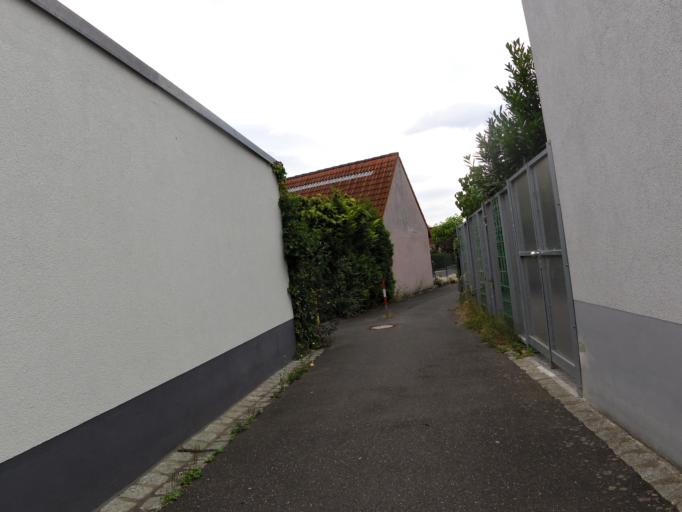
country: DE
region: Bavaria
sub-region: Regierungsbezirk Unterfranken
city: Eibelstadt
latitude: 49.7241
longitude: 9.9730
